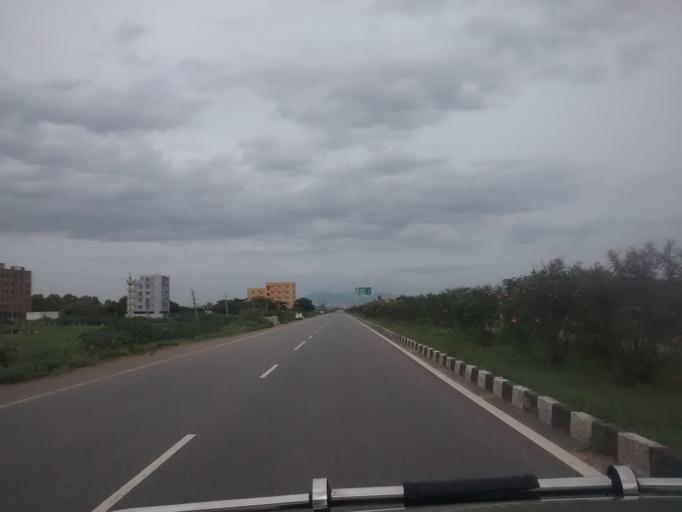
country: IN
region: Andhra Pradesh
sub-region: Chittoor
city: Tirupati
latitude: 13.6046
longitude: 79.3914
